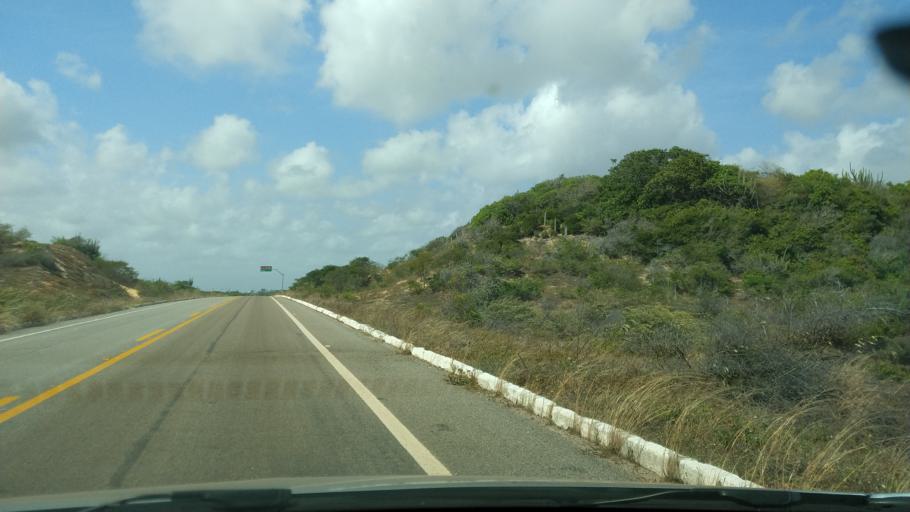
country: BR
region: Rio Grande do Norte
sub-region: Touros
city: Touros
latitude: -5.1681
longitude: -35.5051
